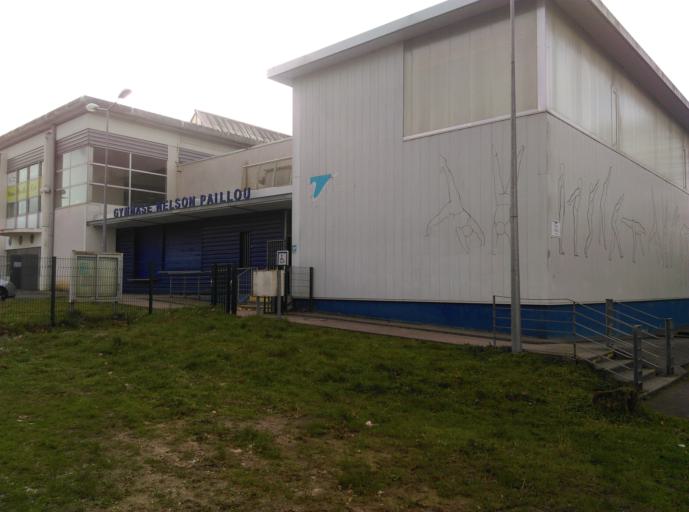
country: FR
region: Aquitaine
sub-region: Departement de la Gironde
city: Villenave-d'Ornon
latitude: 44.7805
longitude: -0.5667
